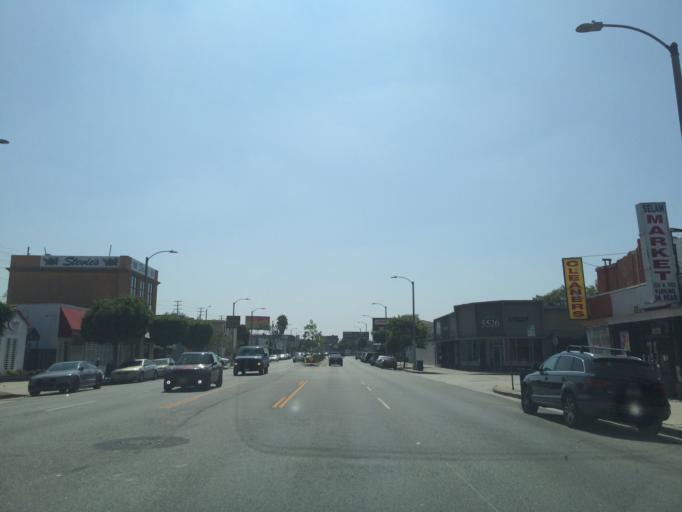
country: US
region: California
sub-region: Los Angeles County
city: West Hollywood
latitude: 34.0496
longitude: -118.3594
